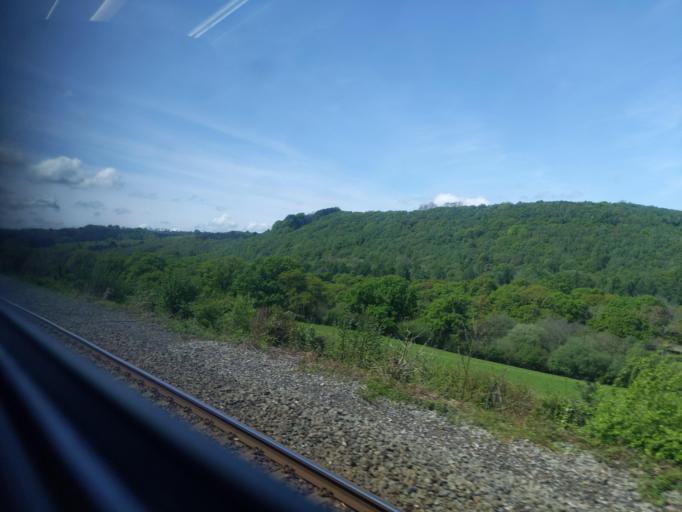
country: GB
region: England
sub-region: Cornwall
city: Lostwithiel
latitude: 50.4572
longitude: -4.6169
